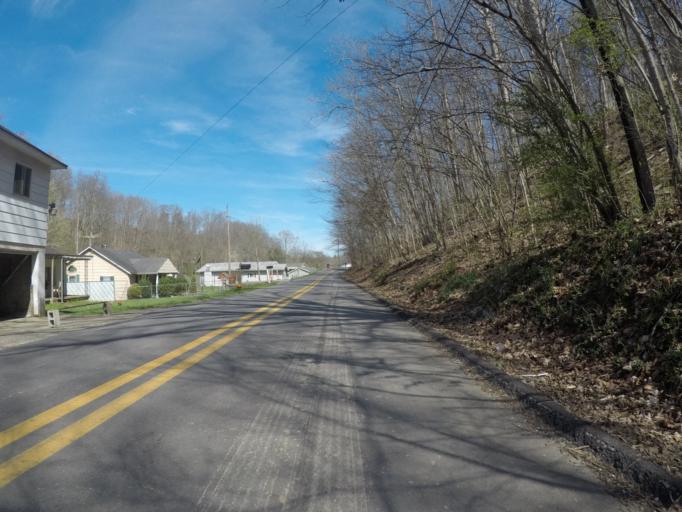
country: US
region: West Virginia
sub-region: Cabell County
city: Pea Ridge
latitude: 38.4009
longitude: -82.3493
